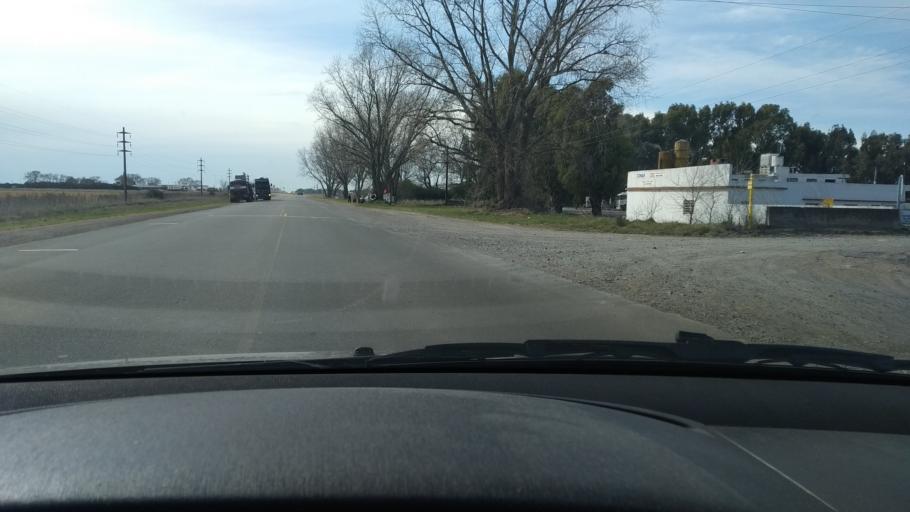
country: AR
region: Buenos Aires
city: Olavarria
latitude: -36.9407
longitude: -60.2349
